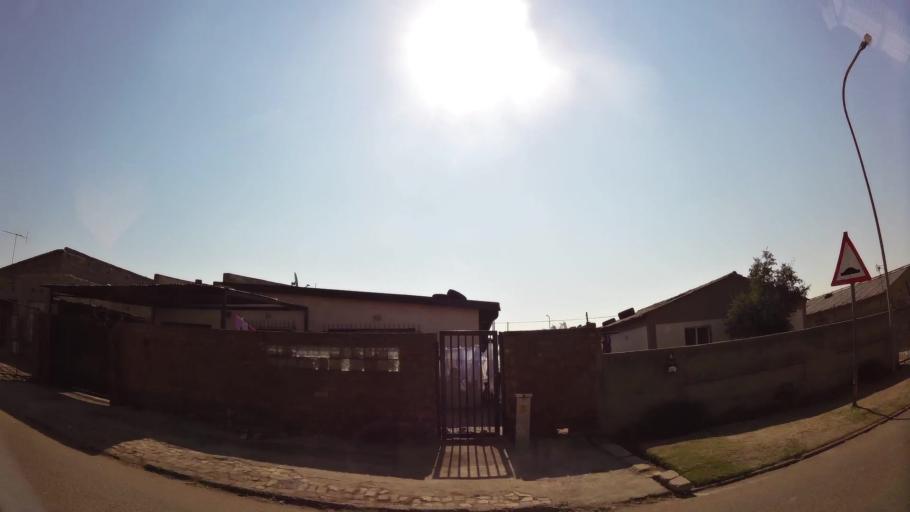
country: ZA
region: Gauteng
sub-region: Ekurhuleni Metropolitan Municipality
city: Benoni
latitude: -26.2210
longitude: 28.3066
